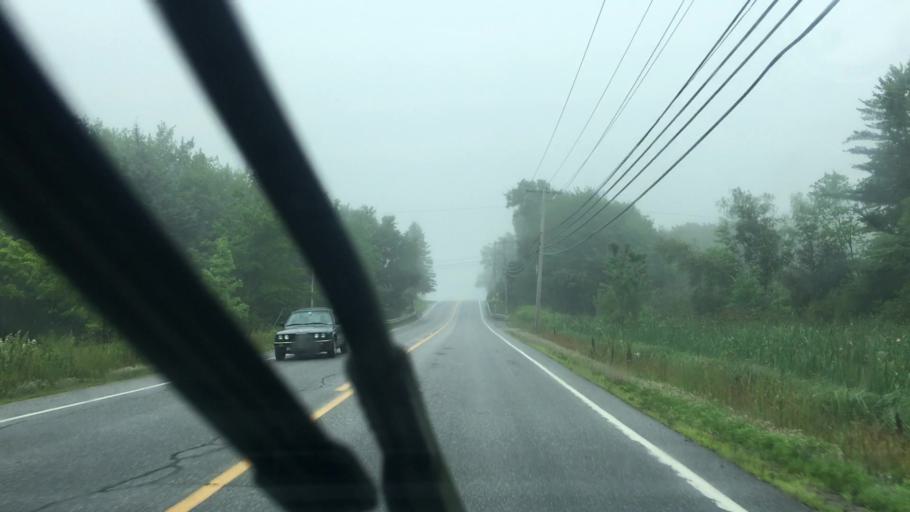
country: US
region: Maine
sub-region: Lincoln County
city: Boothbay
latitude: 43.8706
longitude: -69.6314
